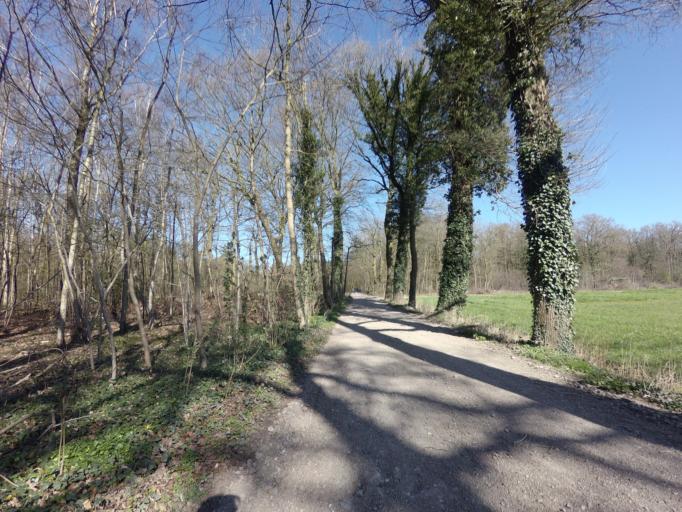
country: NL
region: Utrecht
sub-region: Gemeente Utrechtse Heuvelrug
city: Doorn
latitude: 52.0291
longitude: 5.3262
